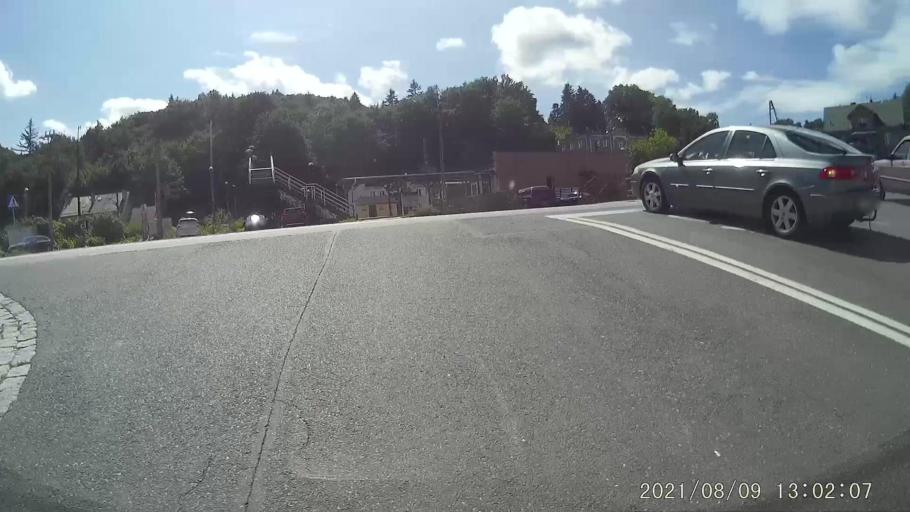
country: PL
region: Lower Silesian Voivodeship
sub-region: Powiat zabkowicki
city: Bardo
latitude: 50.5053
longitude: 16.7345
